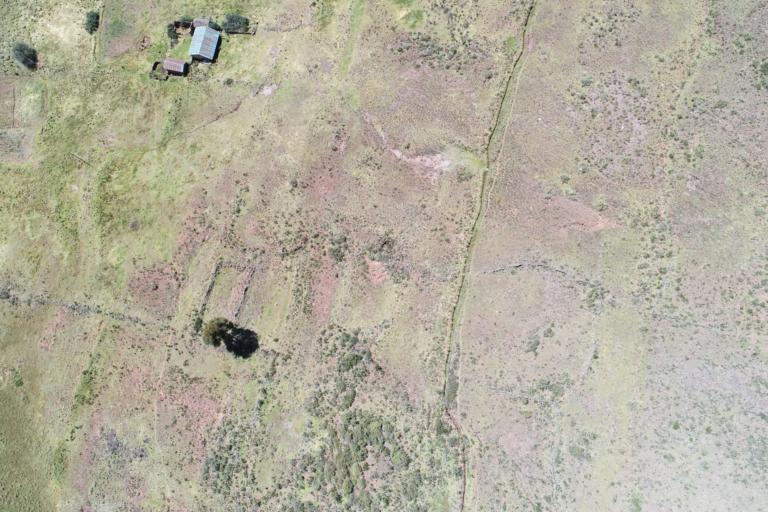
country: BO
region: La Paz
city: Tiahuanaco
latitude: -16.6093
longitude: -68.7628
